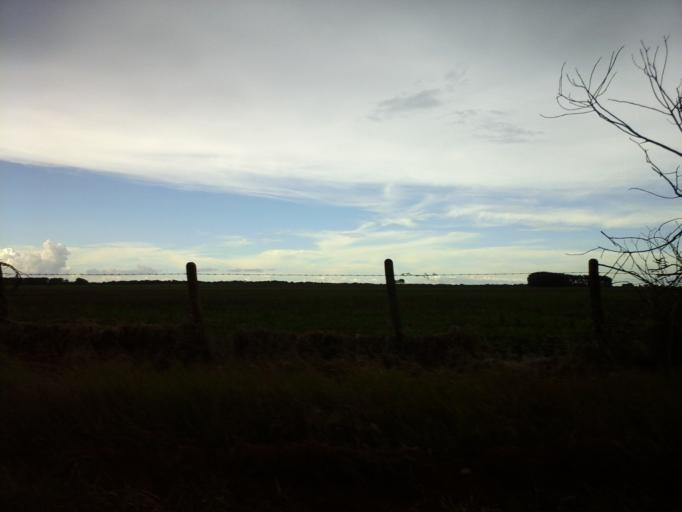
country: CO
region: Cundinamarca
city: Tibacuy
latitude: 4.1984
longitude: -72.4437
